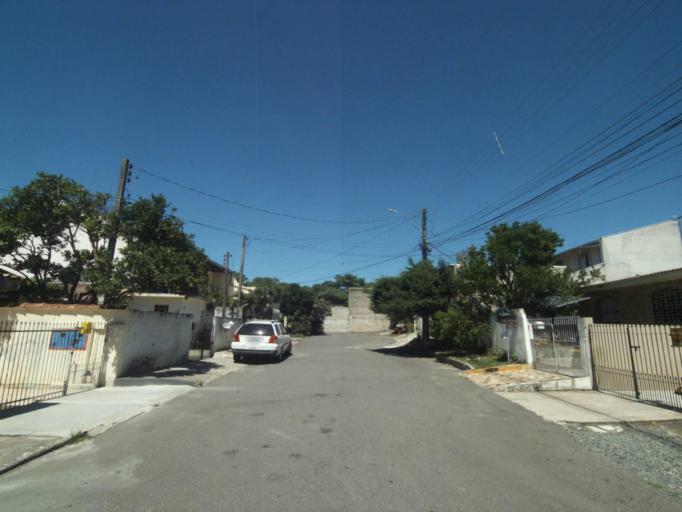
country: BR
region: Parana
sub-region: Curitiba
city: Curitiba
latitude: -25.4753
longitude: -49.3428
